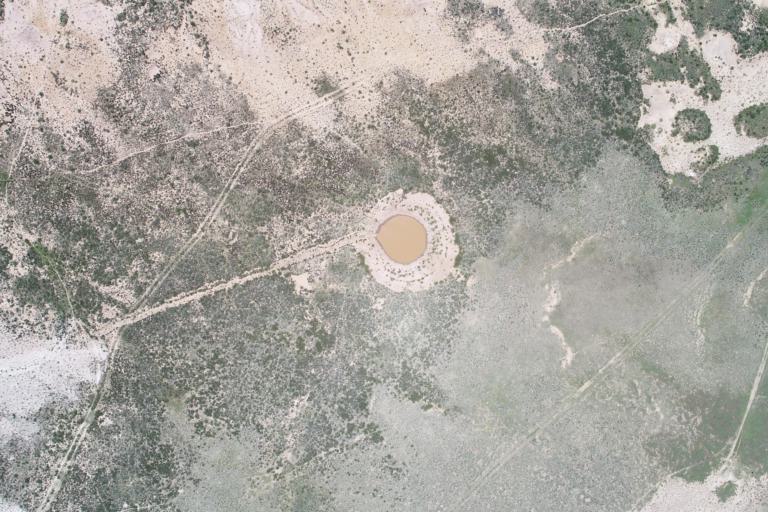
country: BO
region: La Paz
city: Patacamaya
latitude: -17.2807
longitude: -68.4986
